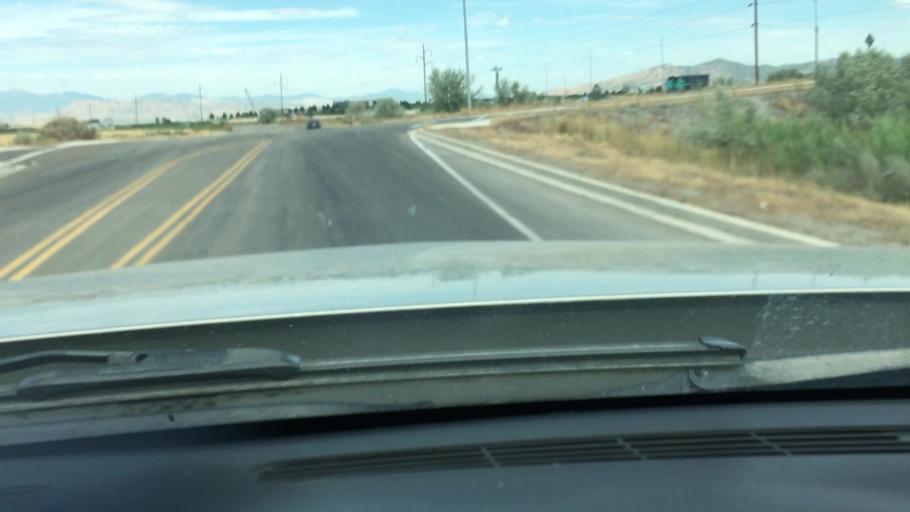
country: US
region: Utah
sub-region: Utah County
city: Pleasant Grove
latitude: 40.3430
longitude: -111.7607
